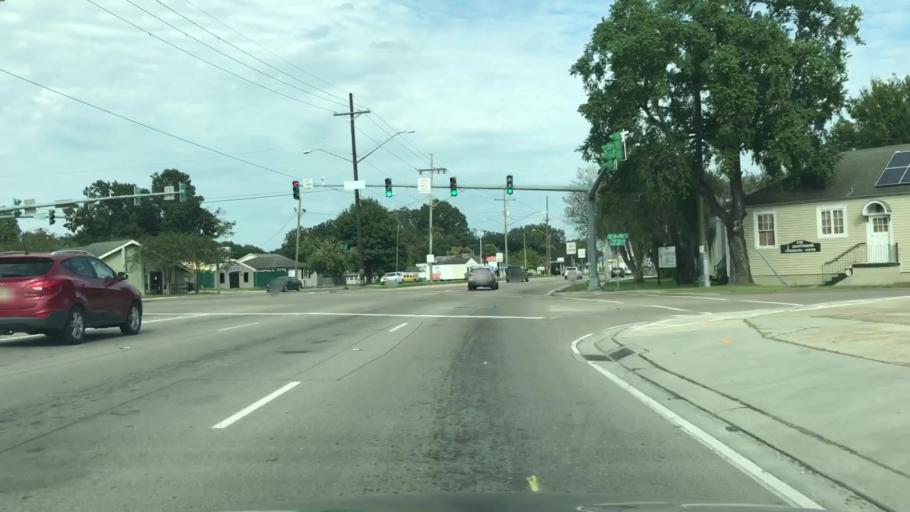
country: US
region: Louisiana
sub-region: Jefferson Parish
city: Elmwood
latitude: 29.9563
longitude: -90.1771
